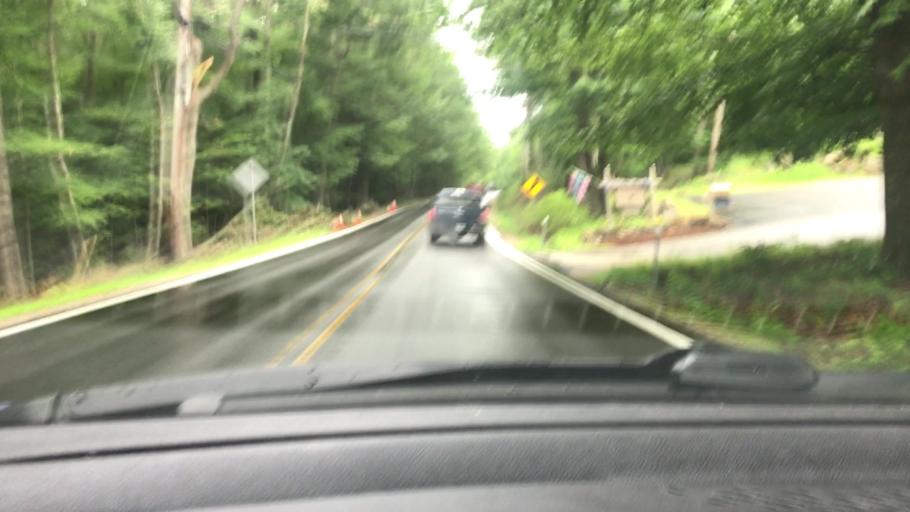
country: US
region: New Hampshire
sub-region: Merrimack County
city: Epsom
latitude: 43.2059
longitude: -71.2763
